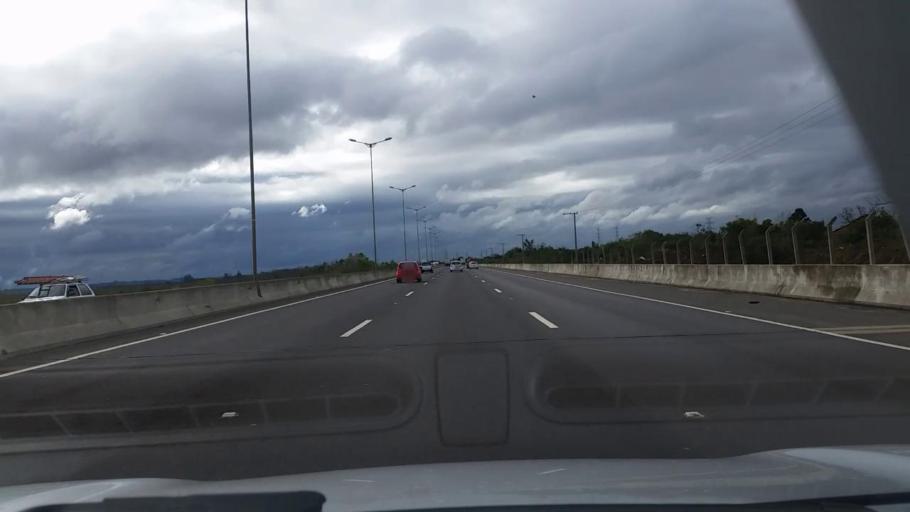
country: BR
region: Rio Grande do Sul
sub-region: Canoas
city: Canoas
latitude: -29.9489
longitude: -51.2036
